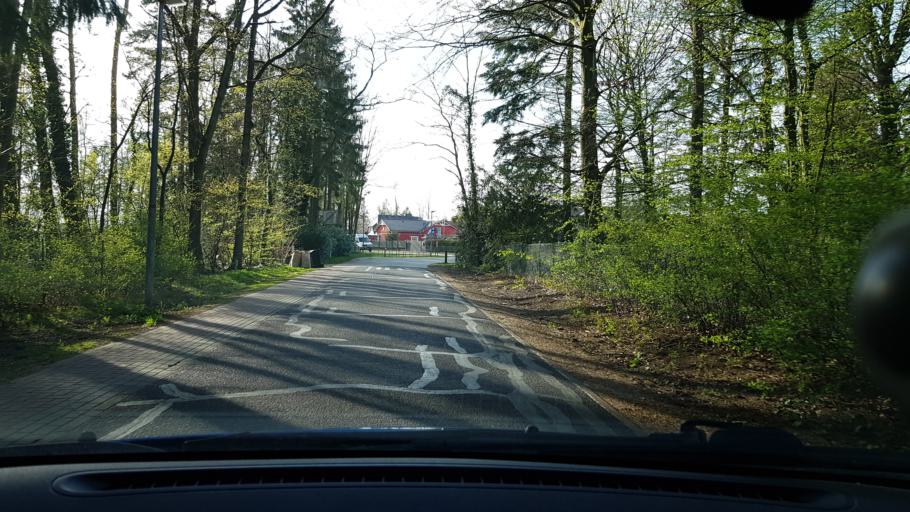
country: DE
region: Lower Saxony
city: Jesteburg
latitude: 53.3131
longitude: 9.9181
